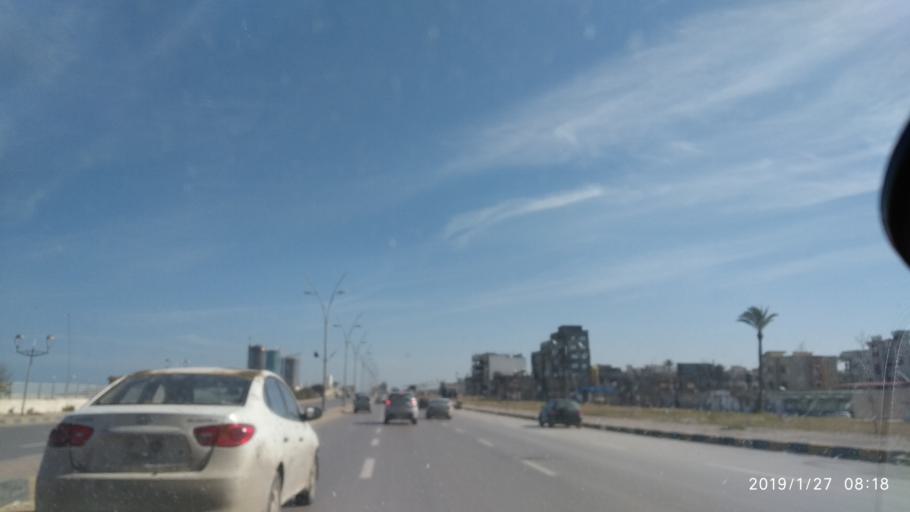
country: LY
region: Tripoli
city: Tripoli
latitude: 32.9069
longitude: 13.2504
